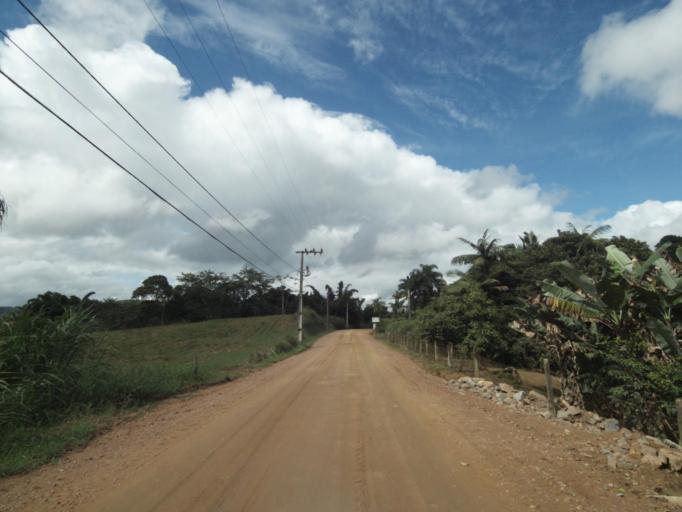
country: BR
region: Santa Catarina
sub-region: Pomerode
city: Pomerode
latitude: -26.6846
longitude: -49.1786
